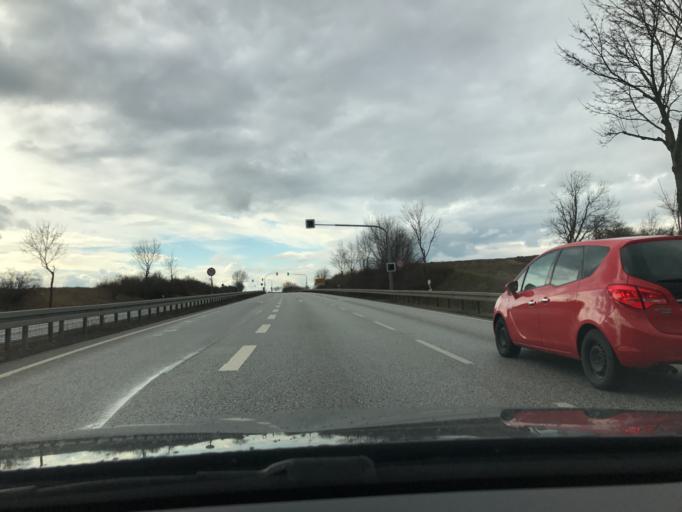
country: DE
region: Saxony-Anhalt
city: Bennstedt
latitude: 51.4796
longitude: 11.8047
